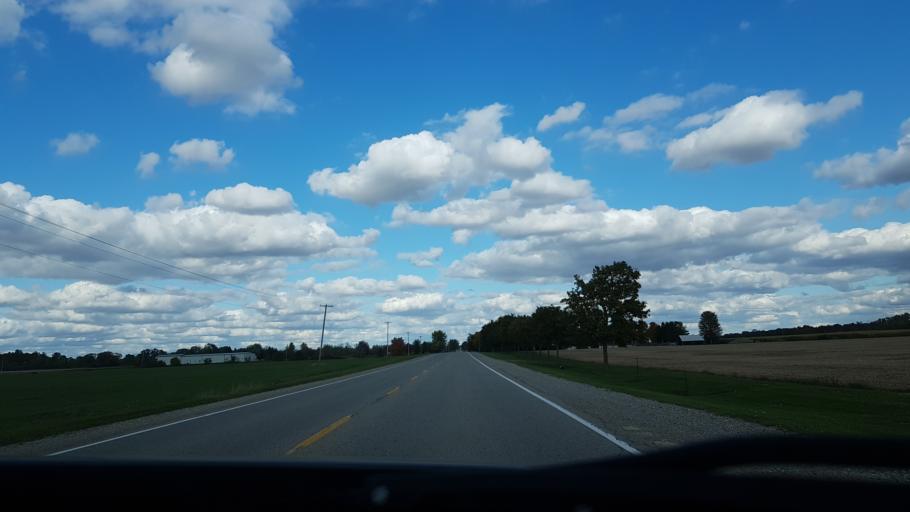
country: CA
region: Ontario
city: South Huron
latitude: 43.0904
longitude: -81.5772
